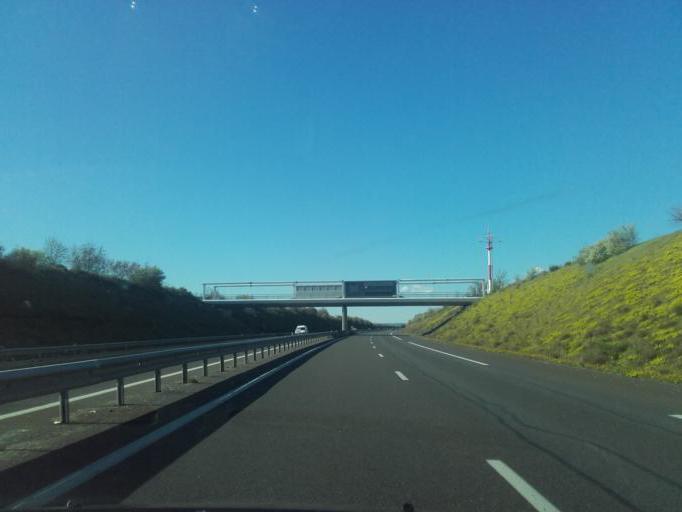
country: FR
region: Rhone-Alpes
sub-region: Departement de l'Isere
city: Janneyrias
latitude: 45.7182
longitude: 5.0973
